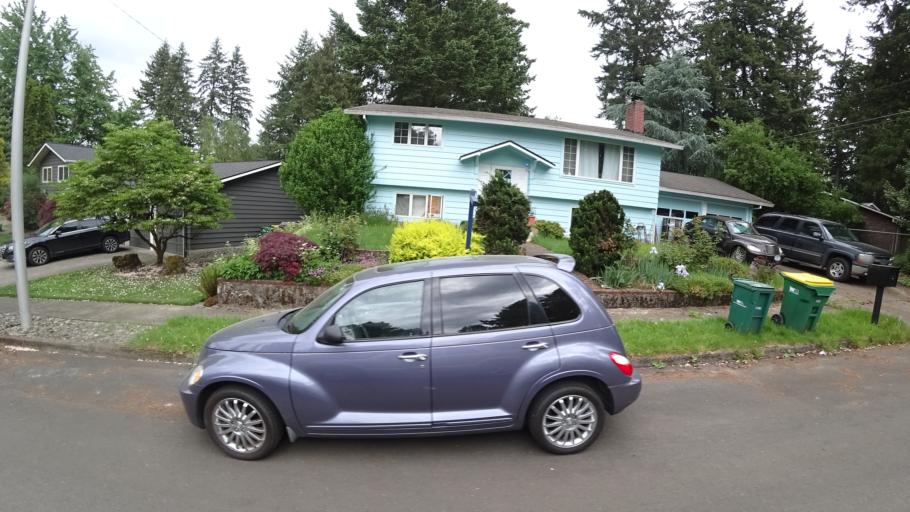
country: US
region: Oregon
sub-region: Washington County
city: Garden Home-Whitford
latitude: 45.4662
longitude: -122.7808
